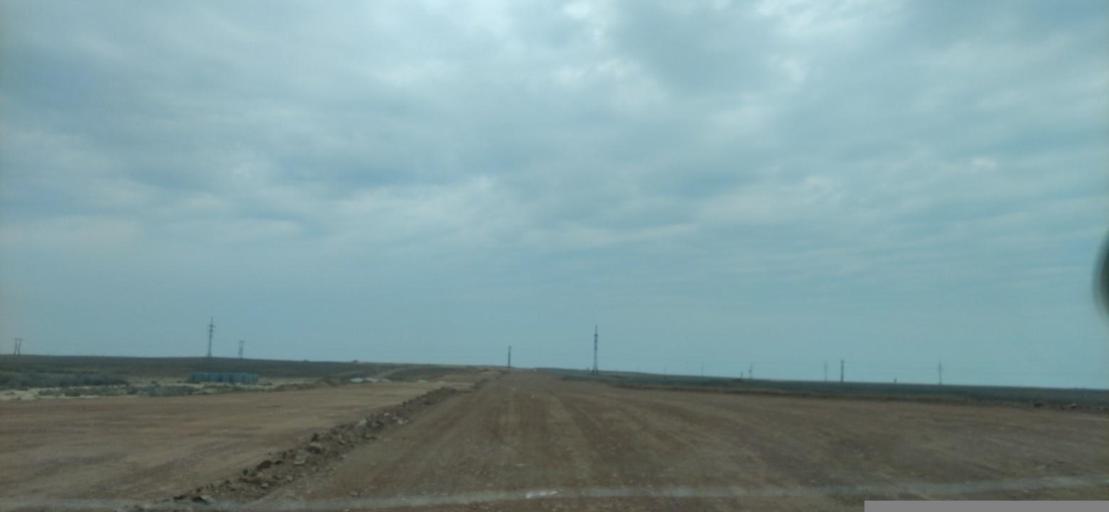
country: KZ
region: Qaraghandy
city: Saryshaghan
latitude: 46.0584
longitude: 73.5980
